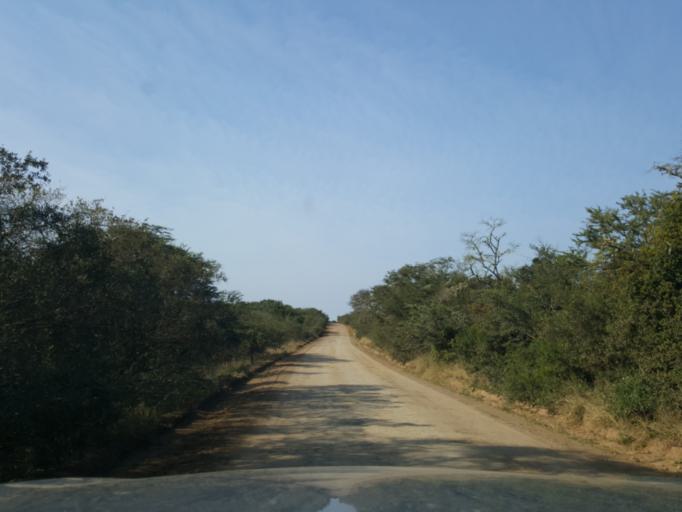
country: ZA
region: Eastern Cape
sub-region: Cacadu District Municipality
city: Grahamstown
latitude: -33.4018
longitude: 26.2920
